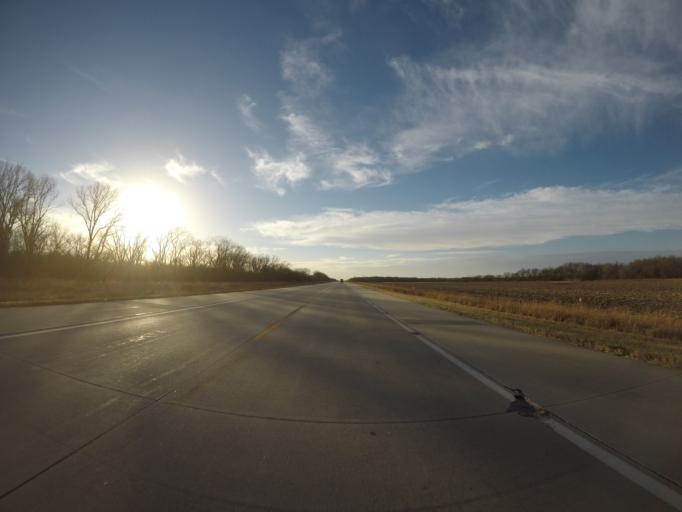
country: US
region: Kansas
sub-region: Lyon County
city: Emporia
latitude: 38.4065
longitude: -96.3101
